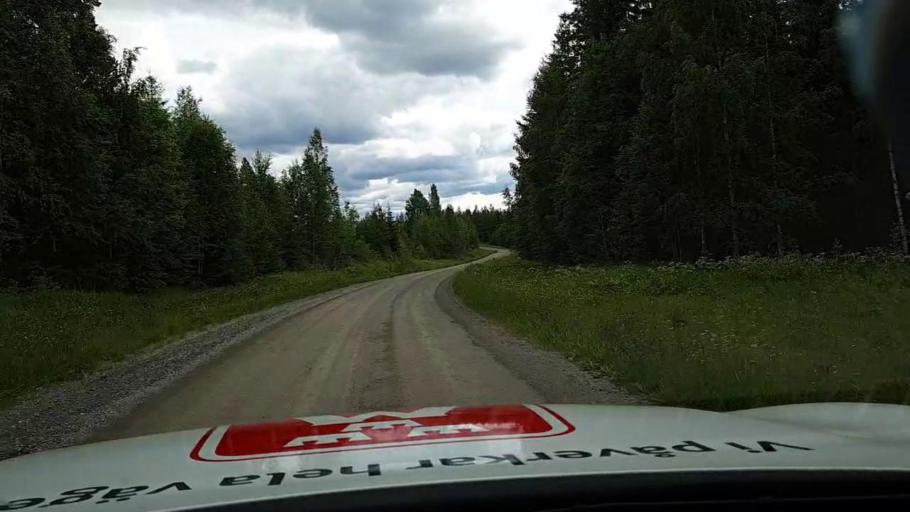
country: SE
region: Jaemtland
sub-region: Braecke Kommun
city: Braecke
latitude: 63.2196
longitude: 15.3485
